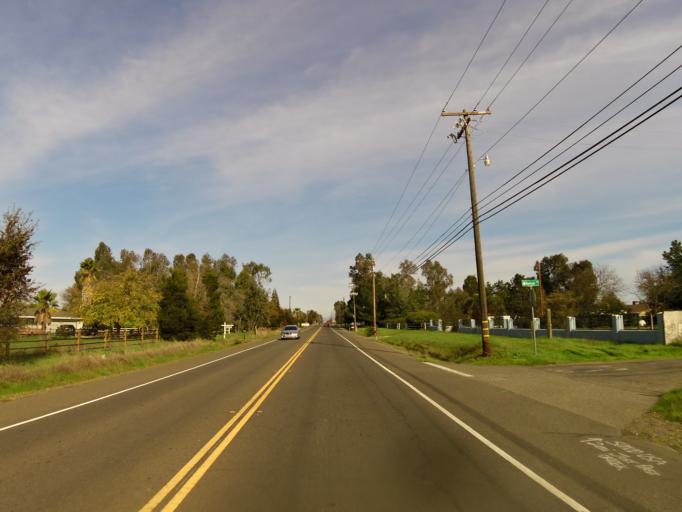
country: US
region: California
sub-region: Sacramento County
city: Wilton
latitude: 38.4424
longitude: -121.2878
